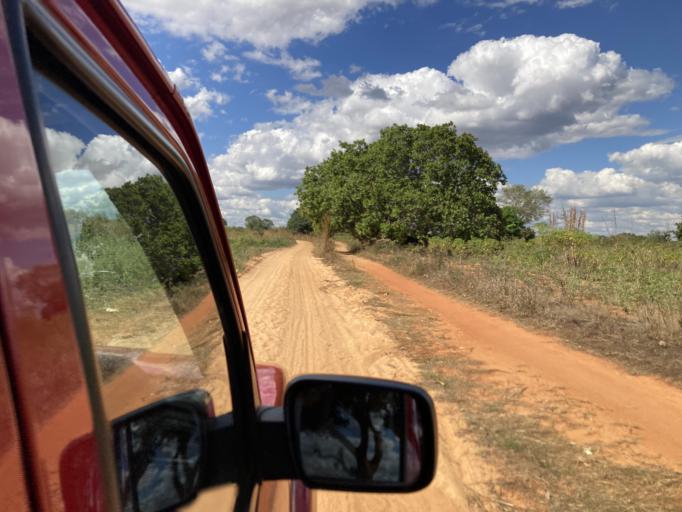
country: MZ
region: Cabo Delgado
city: Montepuez
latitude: -13.1257
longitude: 39.0456
